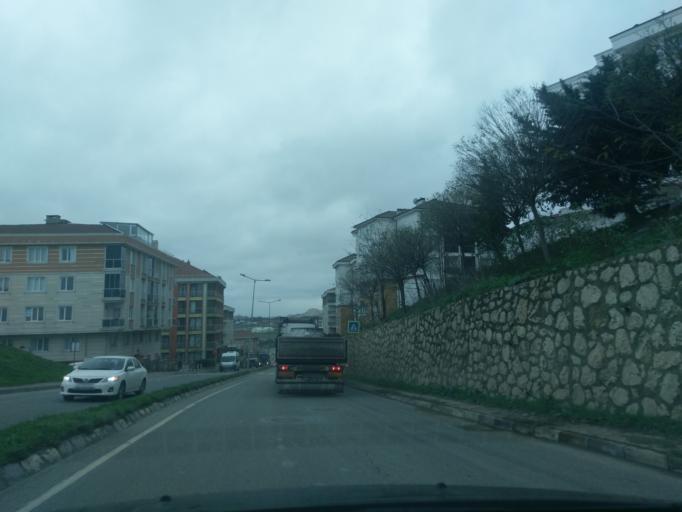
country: TR
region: Istanbul
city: Catalca
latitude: 41.1431
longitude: 28.4690
